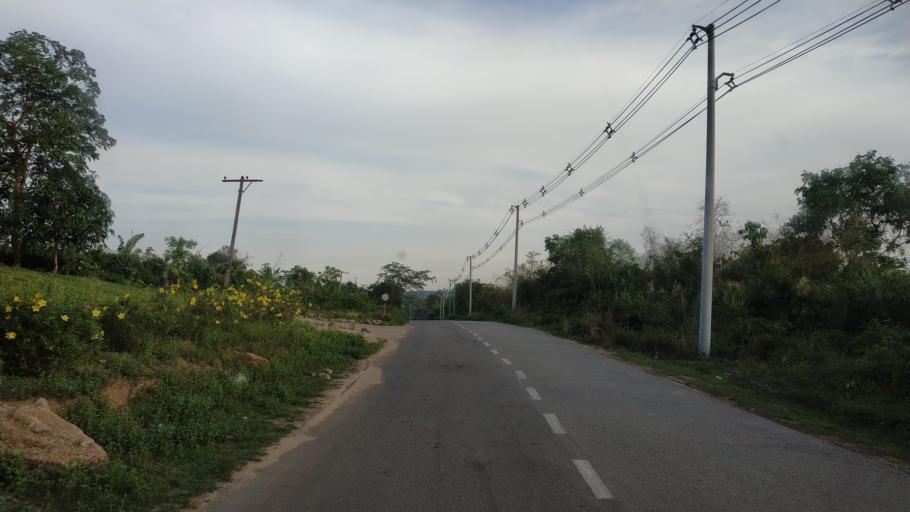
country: MM
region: Mon
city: Kyaikto
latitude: 17.4111
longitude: 97.0727
